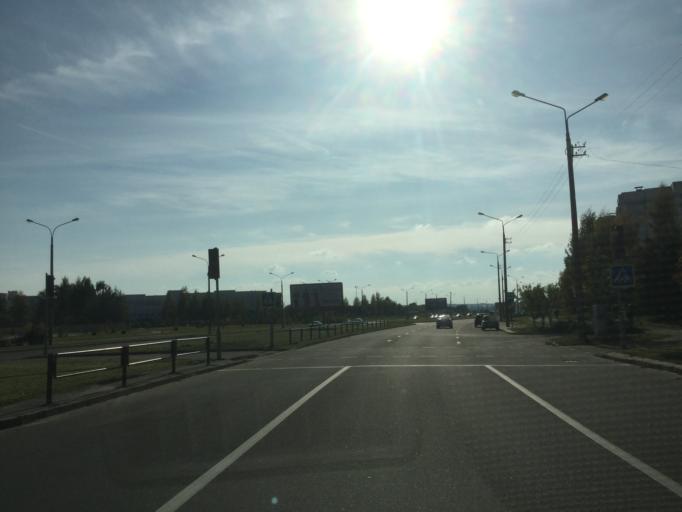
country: BY
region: Vitebsk
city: Vitebsk
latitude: 55.1592
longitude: 30.2188
